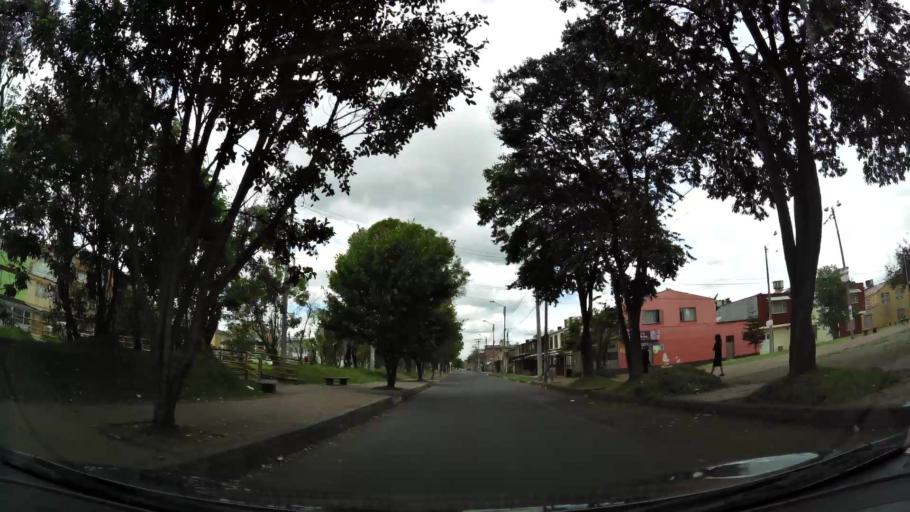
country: CO
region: Bogota D.C.
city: Bogota
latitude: 4.6961
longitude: -74.1197
